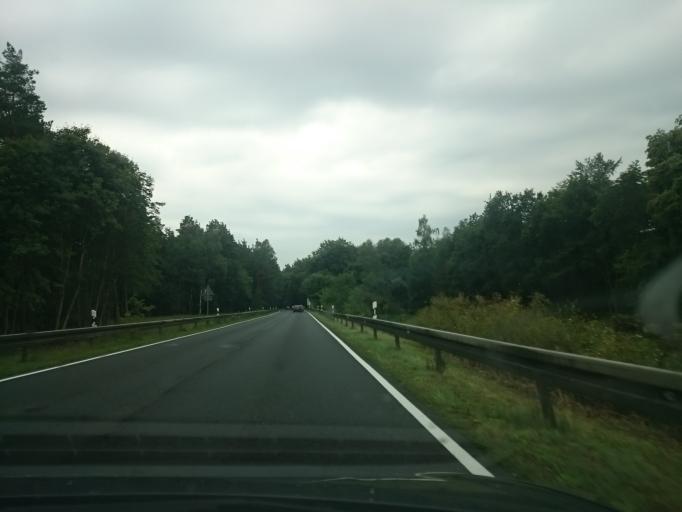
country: DE
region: Brandenburg
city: Gransee
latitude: 53.0884
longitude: 13.1839
